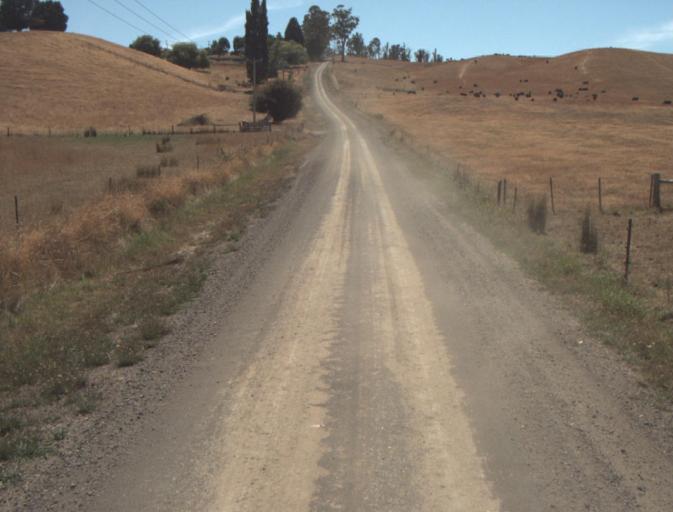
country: AU
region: Tasmania
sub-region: Launceston
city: Mayfield
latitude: -41.2532
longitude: 147.1335
